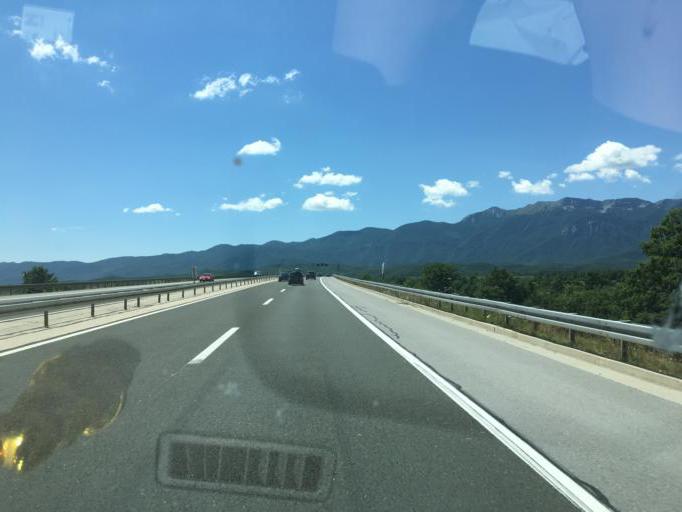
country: HR
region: Zadarska
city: Obrovac
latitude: 44.4041
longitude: 15.6376
